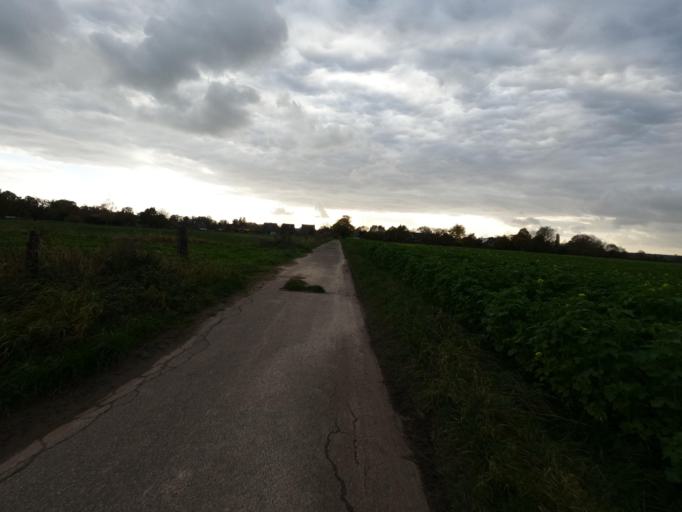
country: DE
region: North Rhine-Westphalia
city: Huckelhoven
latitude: 50.9968
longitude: 6.1867
